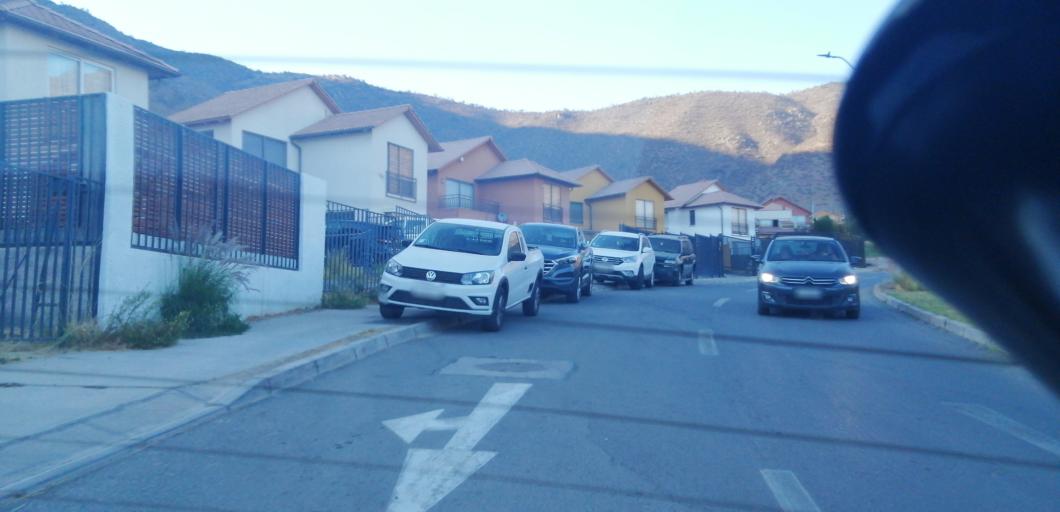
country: CL
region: Santiago Metropolitan
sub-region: Provincia de Santiago
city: Lo Prado
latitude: -33.4585
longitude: -70.8426
